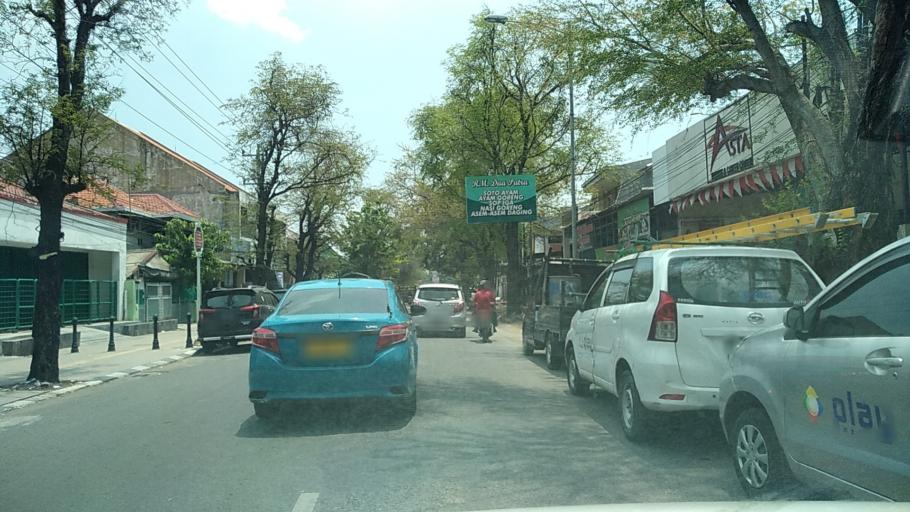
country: ID
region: Central Java
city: Semarang
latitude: -6.9784
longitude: 110.4083
